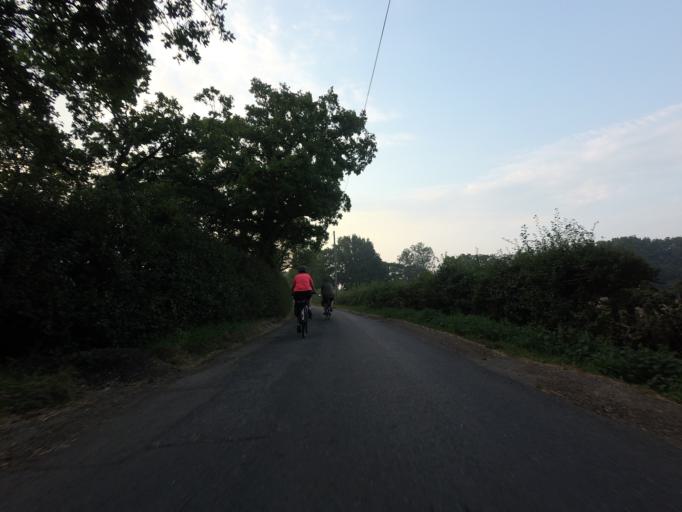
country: GB
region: England
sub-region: Kent
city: Lenham
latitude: 51.1895
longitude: 0.7072
